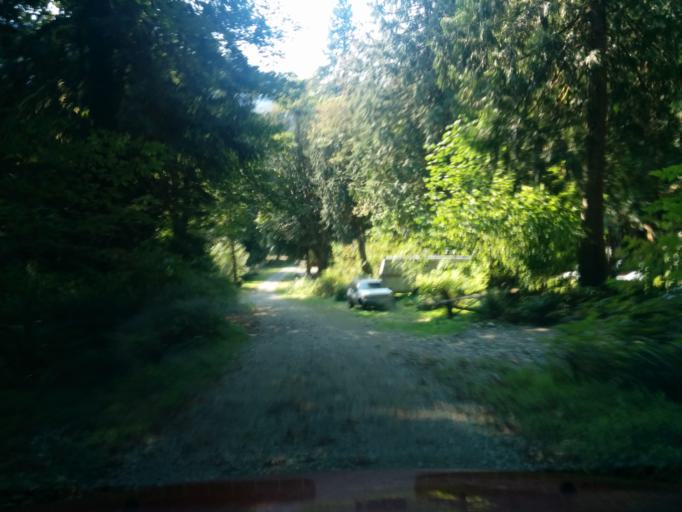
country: US
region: Washington
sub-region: Snohomish County
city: Darrington
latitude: 48.5246
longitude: -121.3457
